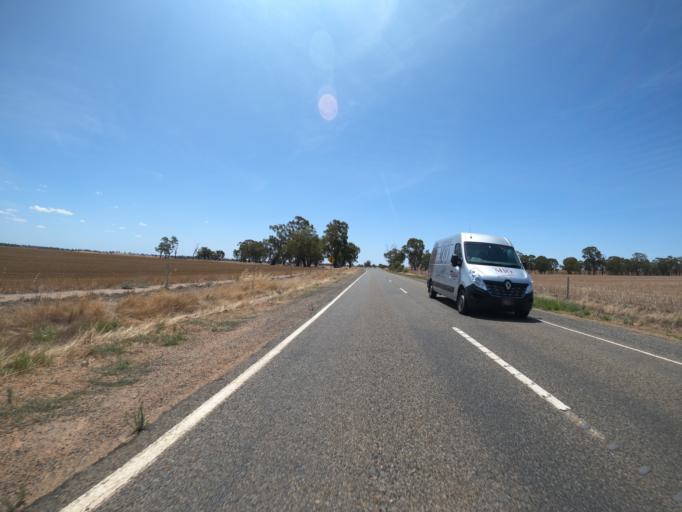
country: AU
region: Victoria
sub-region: Moira
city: Yarrawonga
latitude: -36.1589
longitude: 145.9672
